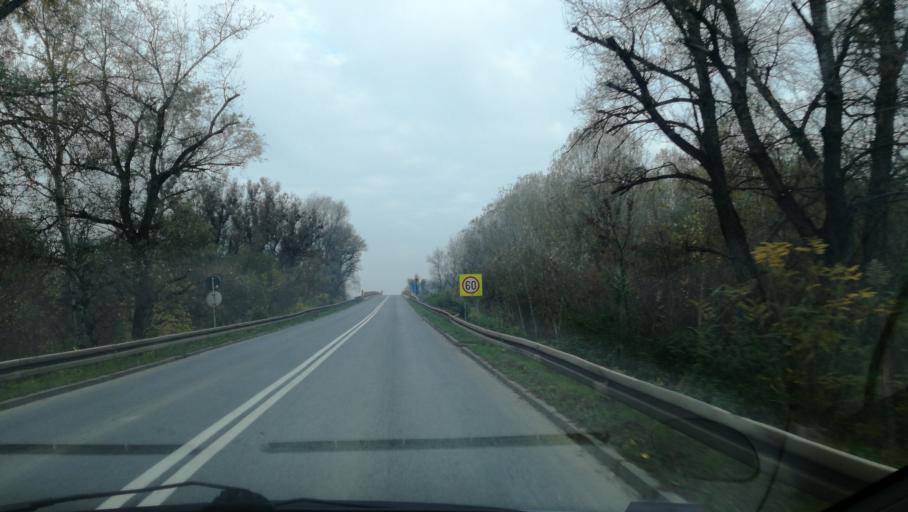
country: RS
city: Taras
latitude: 45.3959
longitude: 20.2161
